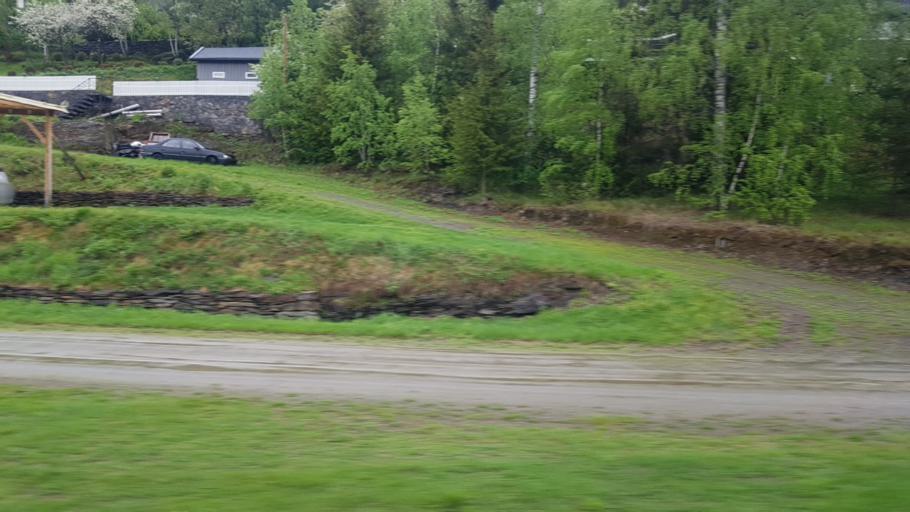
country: NO
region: Oppland
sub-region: Sor-Fron
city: Hundorp
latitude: 61.5718
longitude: 9.8597
